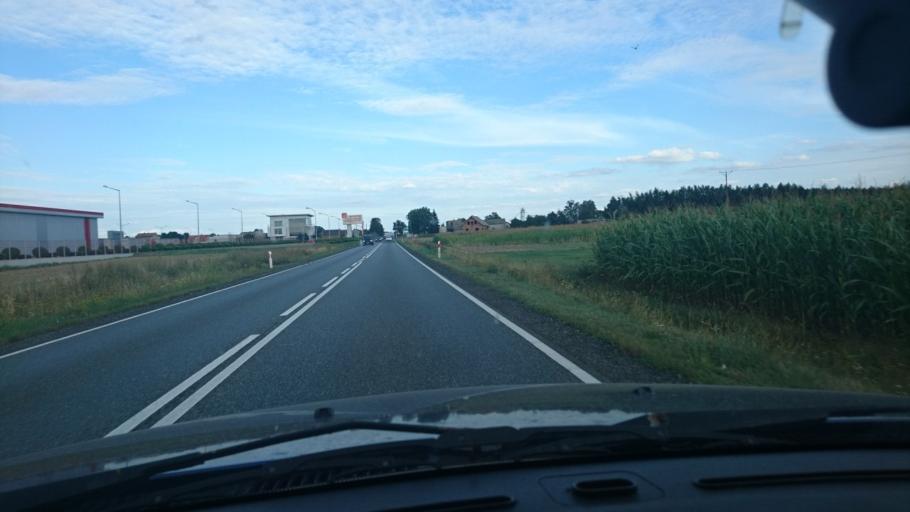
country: PL
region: Greater Poland Voivodeship
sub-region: Powiat kepinski
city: Slupia pod Kepnem
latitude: 51.2315
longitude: 18.0702
